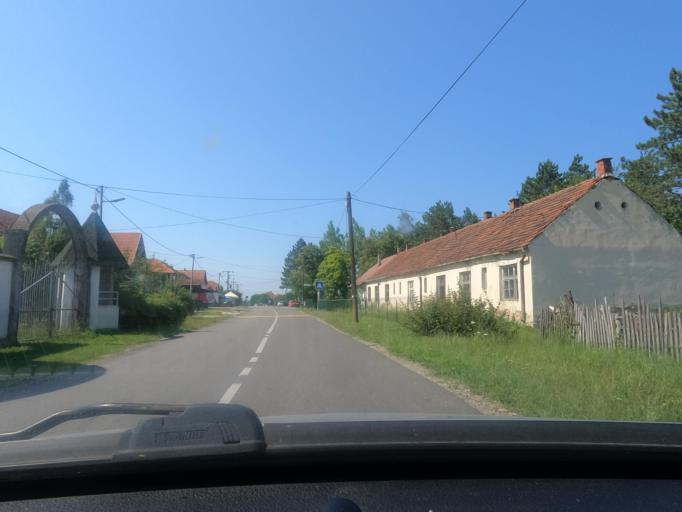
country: RS
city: Kozjak
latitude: 44.5550
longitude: 19.2960
